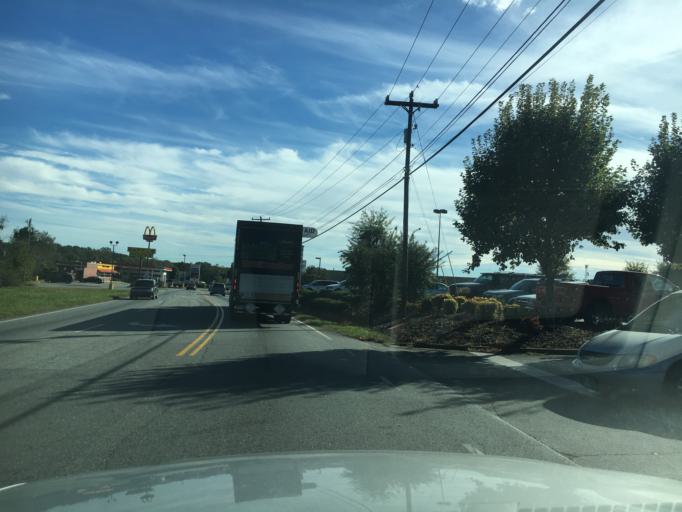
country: US
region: North Carolina
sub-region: Rutherford County
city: Spindale
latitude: 35.3651
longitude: -81.9422
